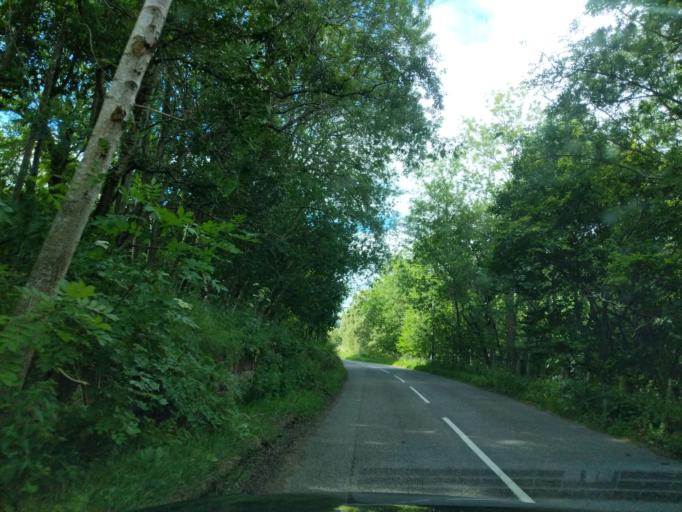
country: GB
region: Scotland
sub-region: Aberdeenshire
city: Ballater
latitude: 57.0588
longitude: -2.9298
